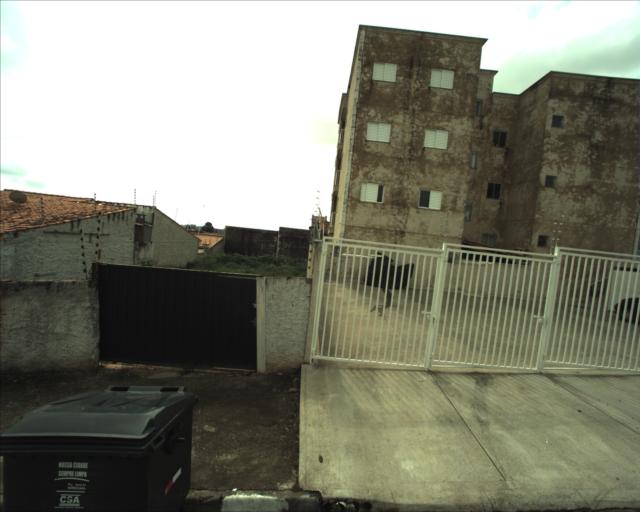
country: BR
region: Sao Paulo
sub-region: Sorocaba
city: Sorocaba
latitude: -23.4993
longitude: -47.4975
